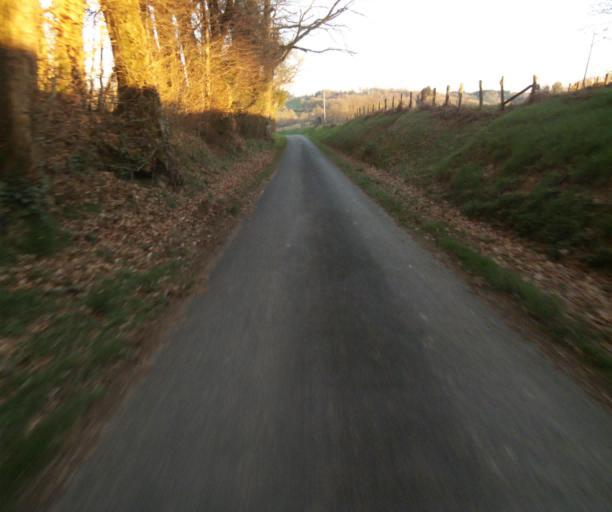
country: FR
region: Limousin
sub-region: Departement de la Correze
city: Uzerche
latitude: 45.3707
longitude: 1.6123
